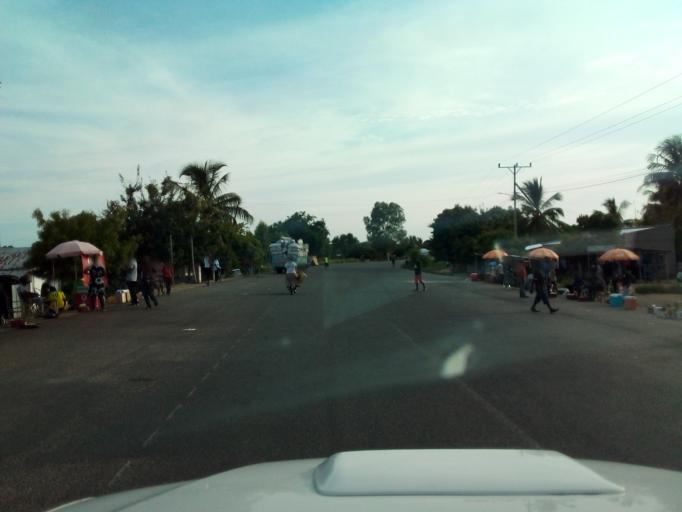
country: MZ
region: Zambezia
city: Quelimane
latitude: -17.4877
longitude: 37.0300
